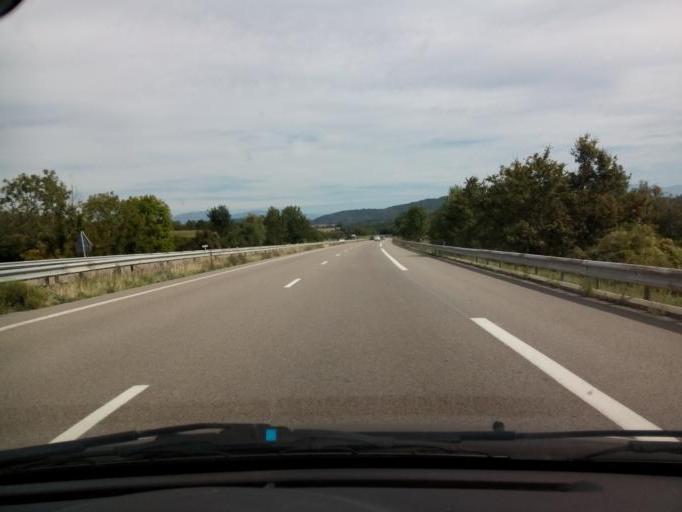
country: FR
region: Rhone-Alpes
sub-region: Departement de l'Isere
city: Chabons
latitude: 45.4432
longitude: 5.4047
